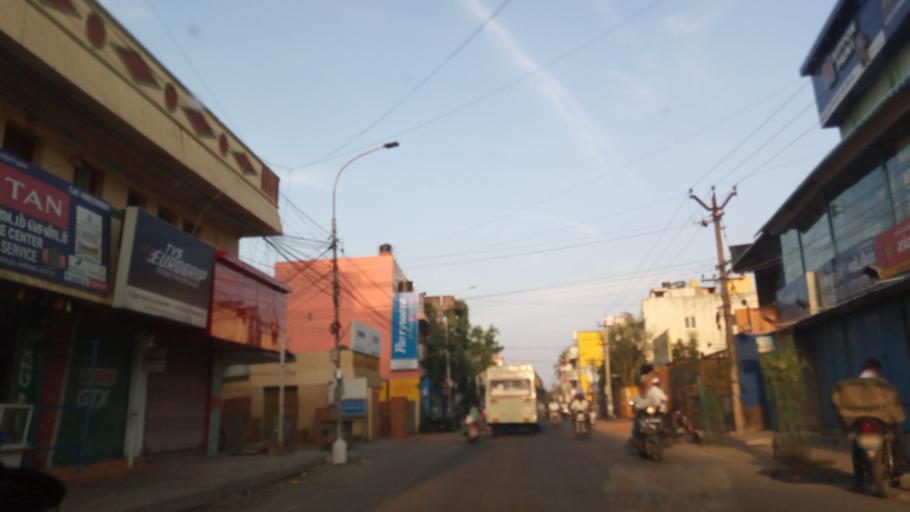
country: IN
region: Tamil Nadu
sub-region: Kancheepuram
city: Manappakkam
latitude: 13.0307
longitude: 80.1837
